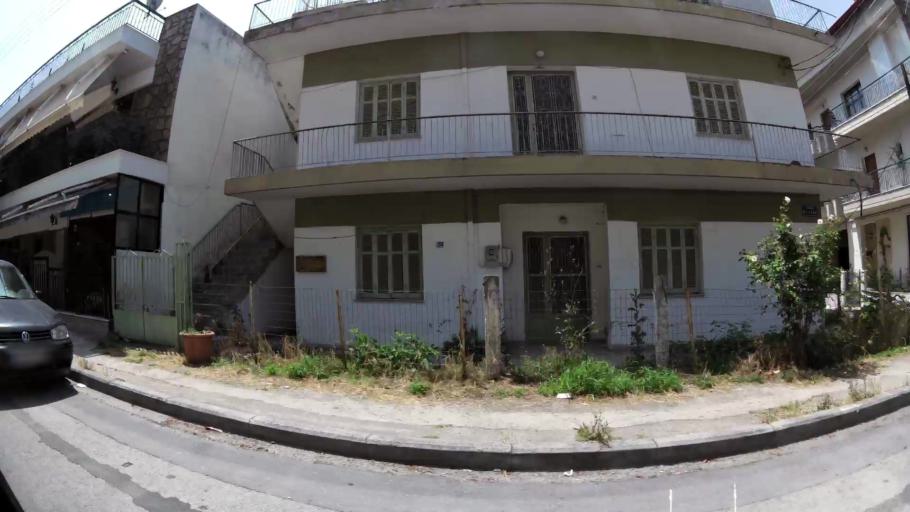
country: GR
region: Central Macedonia
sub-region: Nomos Thessalonikis
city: Evosmos
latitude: 40.6686
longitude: 22.9040
